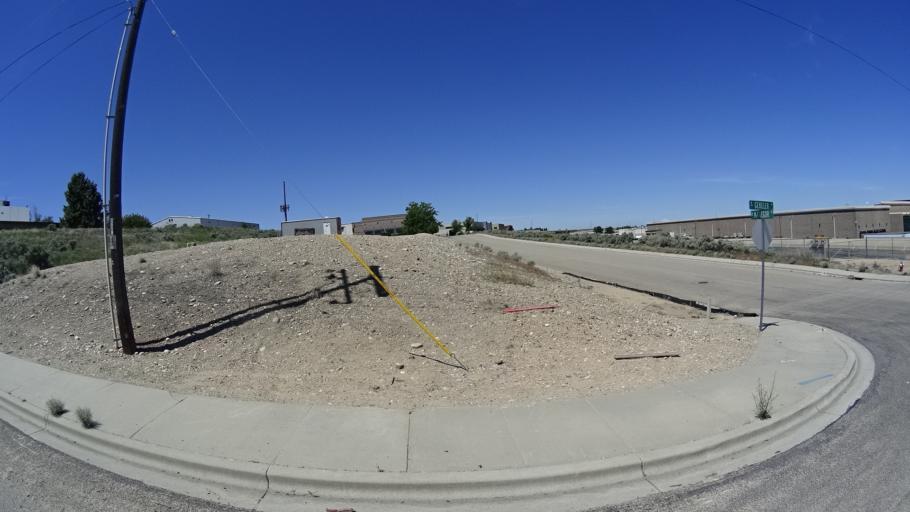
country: US
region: Idaho
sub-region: Ada County
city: Boise
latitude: 43.5662
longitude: -116.1835
